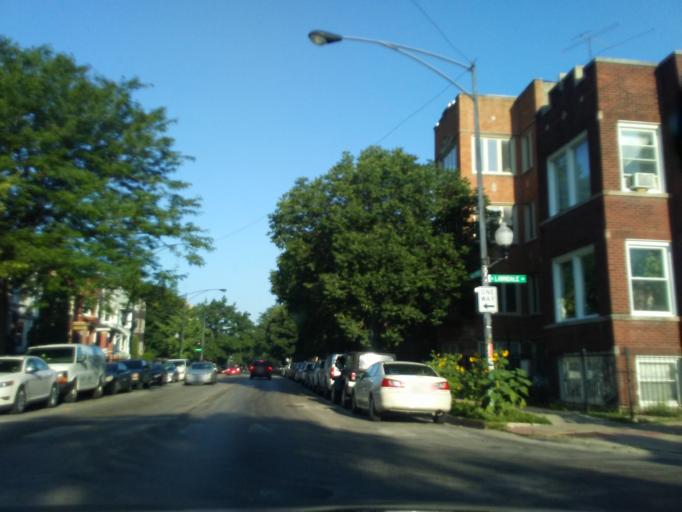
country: US
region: Illinois
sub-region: Cook County
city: Lincolnwood
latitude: 41.9283
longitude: -87.7194
